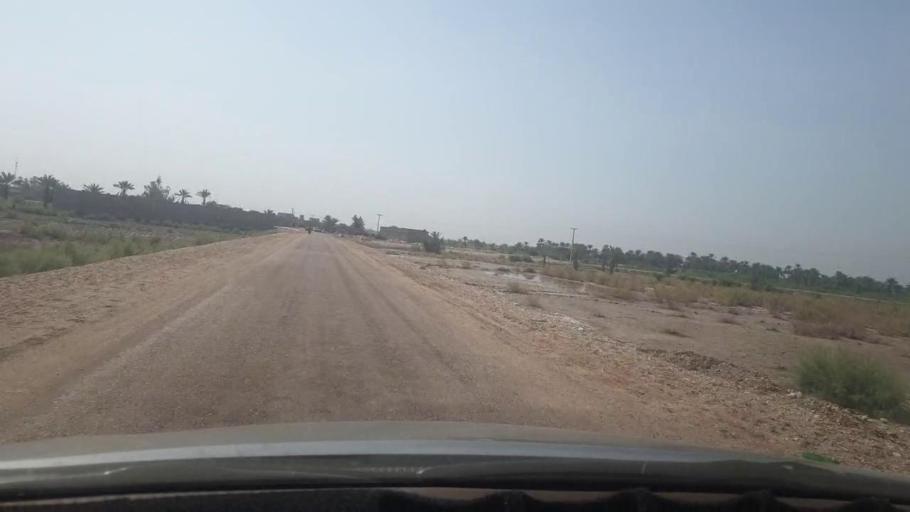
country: PK
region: Sindh
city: Ranipur
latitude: 27.2601
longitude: 68.5865
